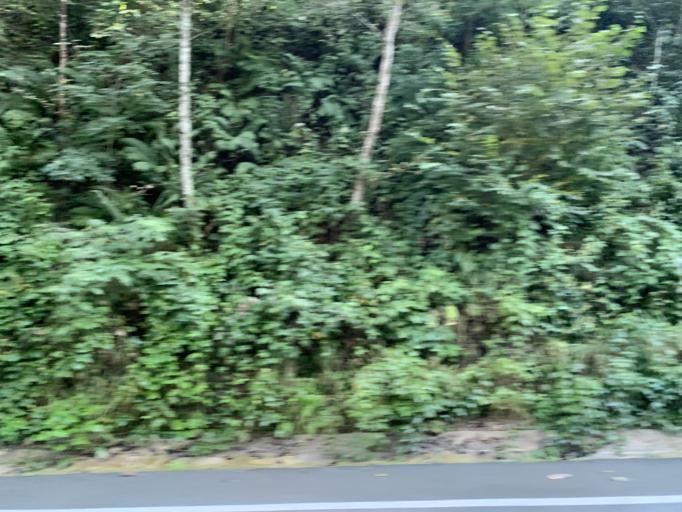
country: TR
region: Trabzon
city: Macka
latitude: 40.7068
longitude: 39.6499
